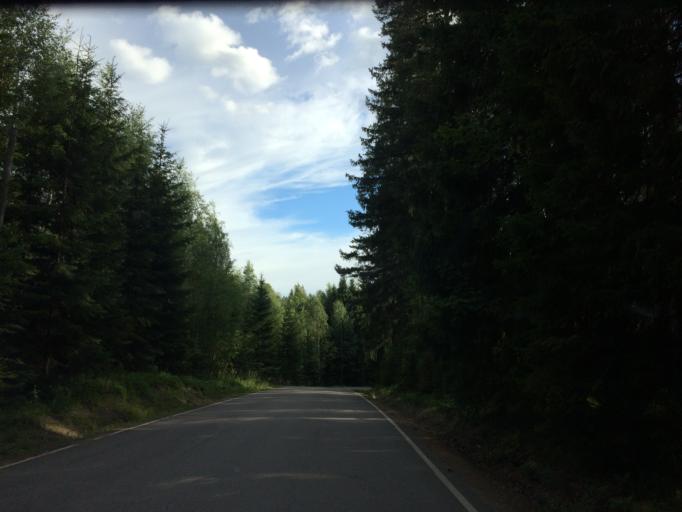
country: FI
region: Haeme
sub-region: Haemeenlinna
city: Janakkala
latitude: 60.8595
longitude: 24.5456
